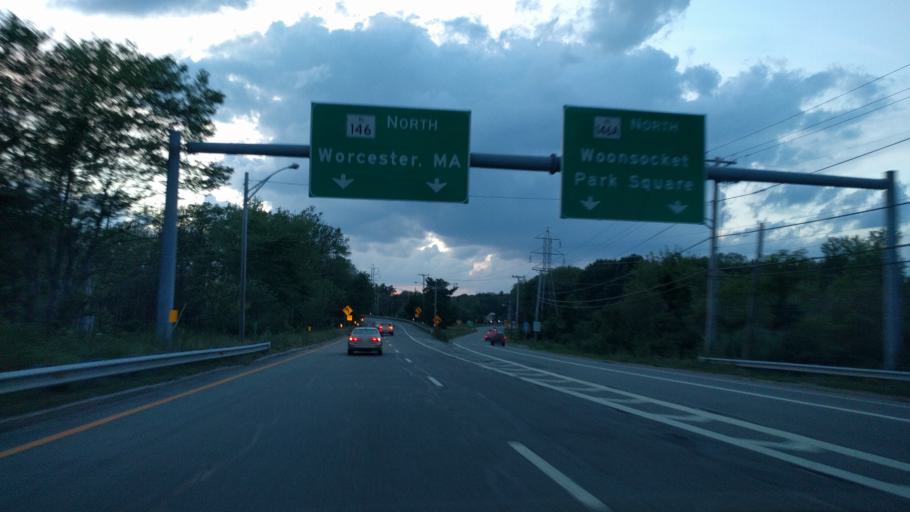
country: US
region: Rhode Island
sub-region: Providence County
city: Woonsocket
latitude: 41.9684
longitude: -71.5049
